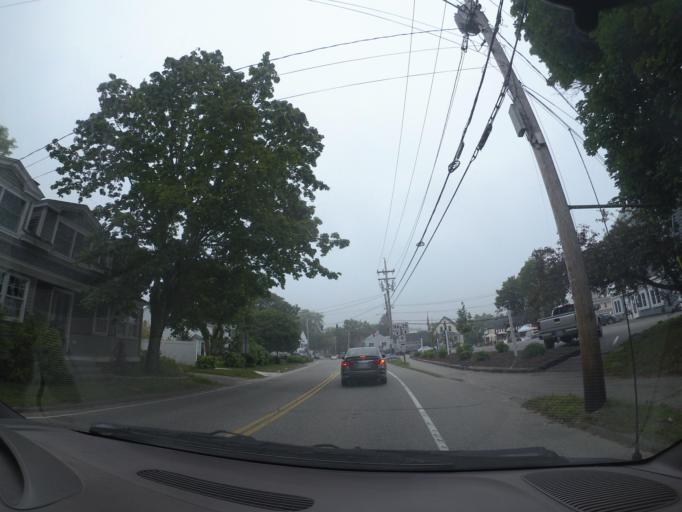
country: US
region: Maine
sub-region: York County
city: Kennebunkport
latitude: 43.3589
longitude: -70.4810
